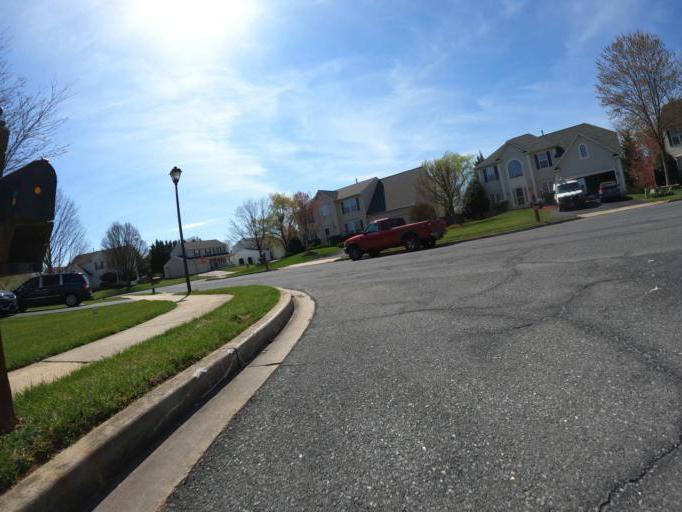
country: US
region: Maryland
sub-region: Frederick County
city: Ballenger Creek
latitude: 39.3849
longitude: -77.4348
